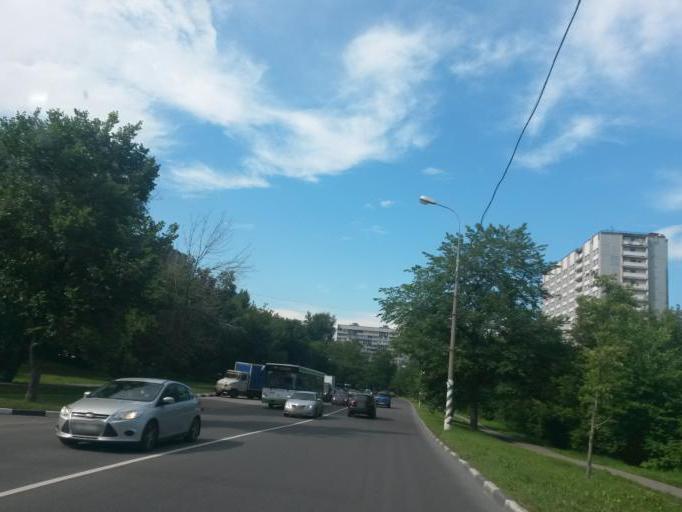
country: RU
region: Moscow
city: Orekhovo-Borisovo
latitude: 55.6224
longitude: 37.7278
